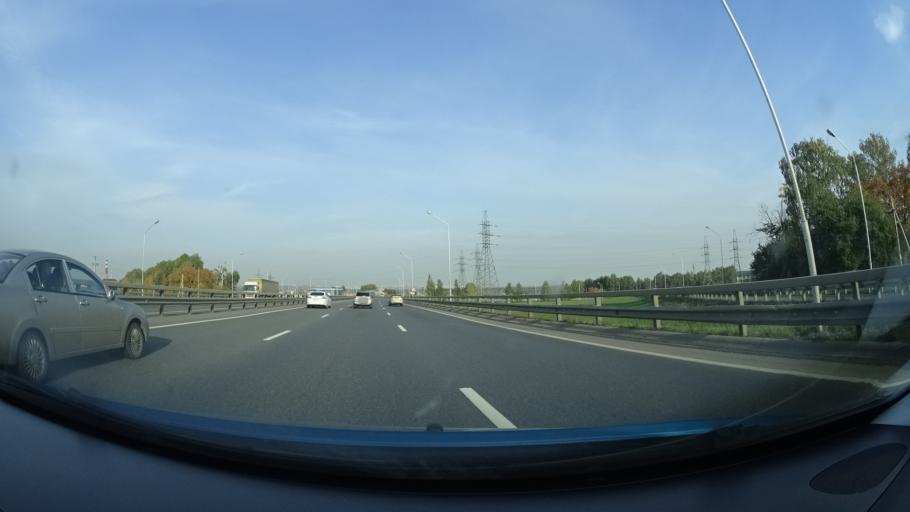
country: RU
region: Bashkortostan
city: Avdon
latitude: 54.6757
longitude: 55.7966
